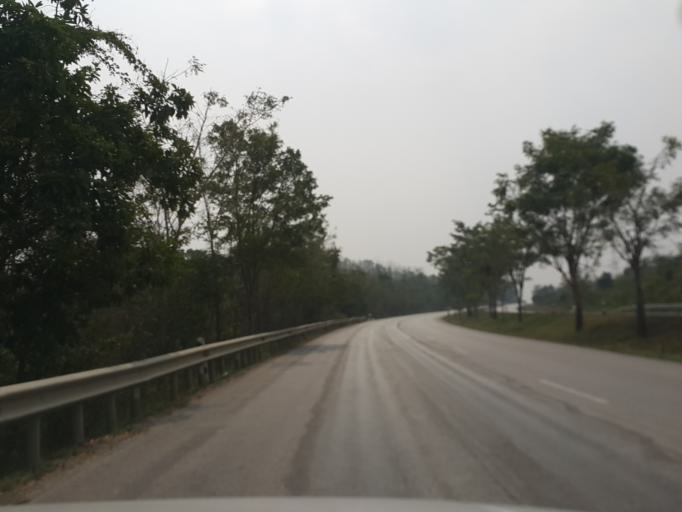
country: TH
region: Lampang
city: Ko Kha
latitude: 18.1012
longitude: 99.3989
